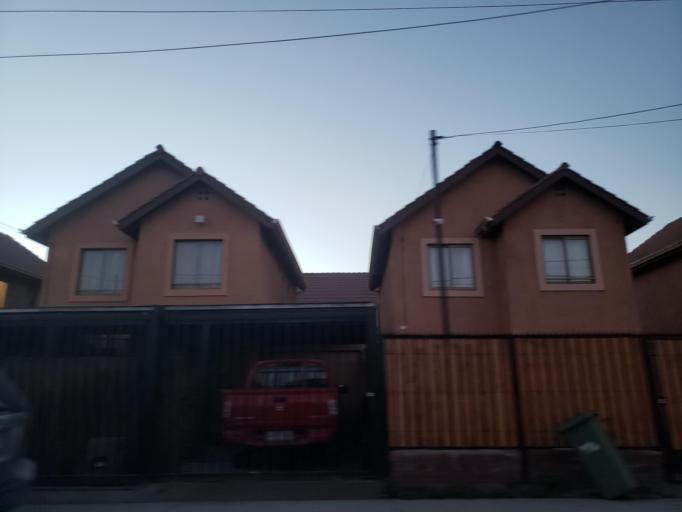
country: CL
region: Santiago Metropolitan
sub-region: Provincia de Talagante
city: Talagante
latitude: -33.6722
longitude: -70.9457
